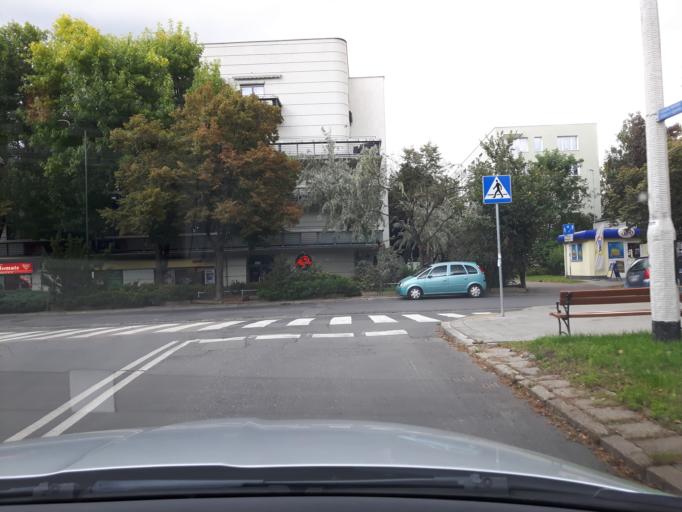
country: PL
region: Masovian Voivodeship
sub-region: Warszawa
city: Praga Poludnie
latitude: 52.2242
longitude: 21.0663
